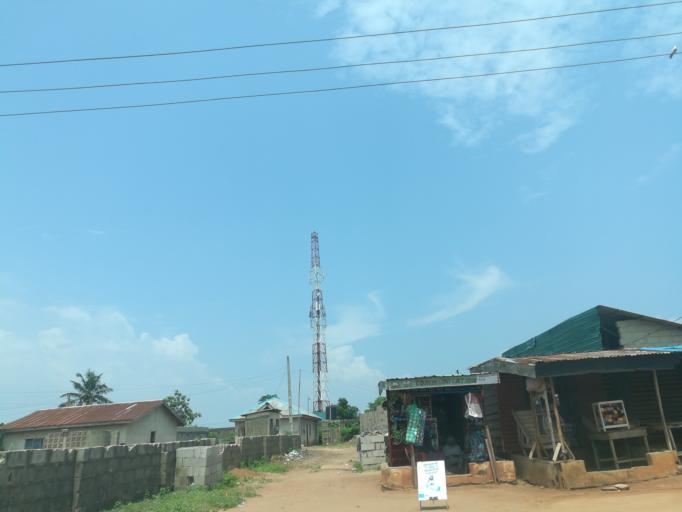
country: NG
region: Lagos
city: Ikorodu
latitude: 6.5786
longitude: 3.6278
